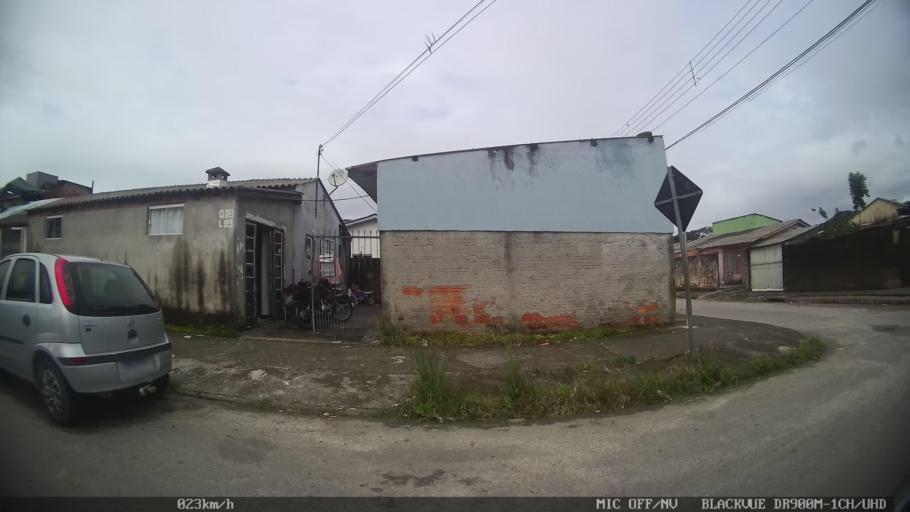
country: BR
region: Santa Catarina
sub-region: Biguacu
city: Biguacu
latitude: -27.5400
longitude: -48.6422
